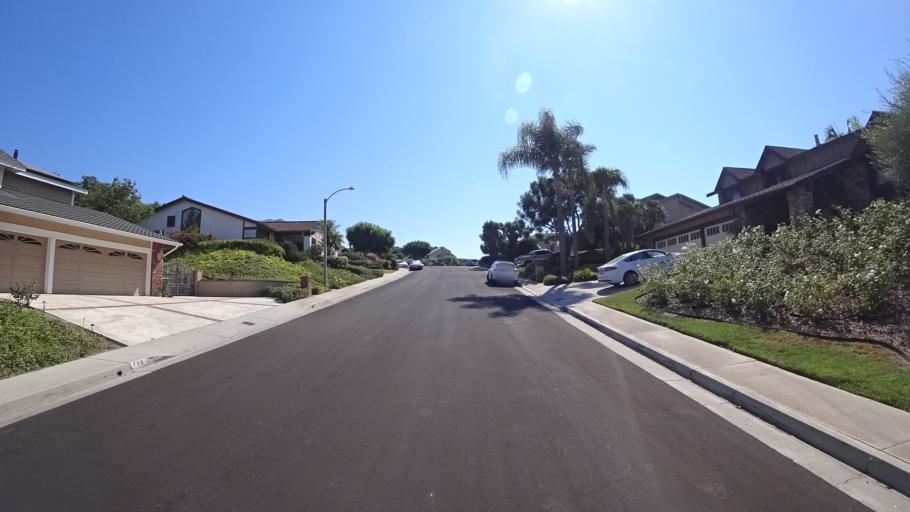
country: US
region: California
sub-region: Orange County
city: San Clemente
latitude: 33.4581
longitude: -117.6373
